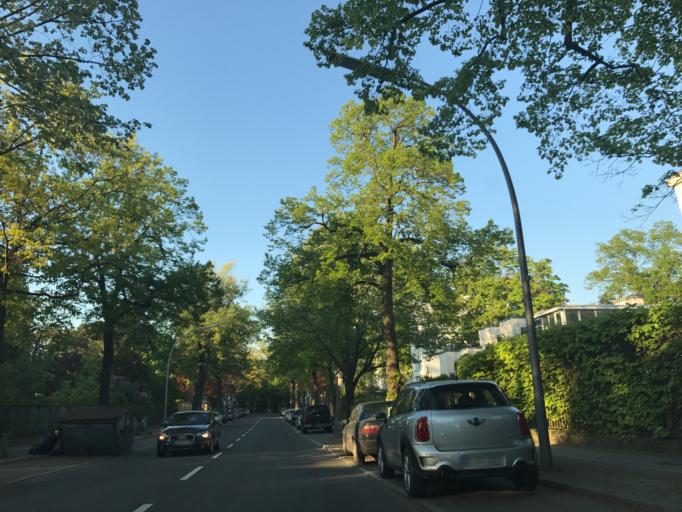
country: DE
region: Berlin
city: Grunewald
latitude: 52.4856
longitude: 13.2696
